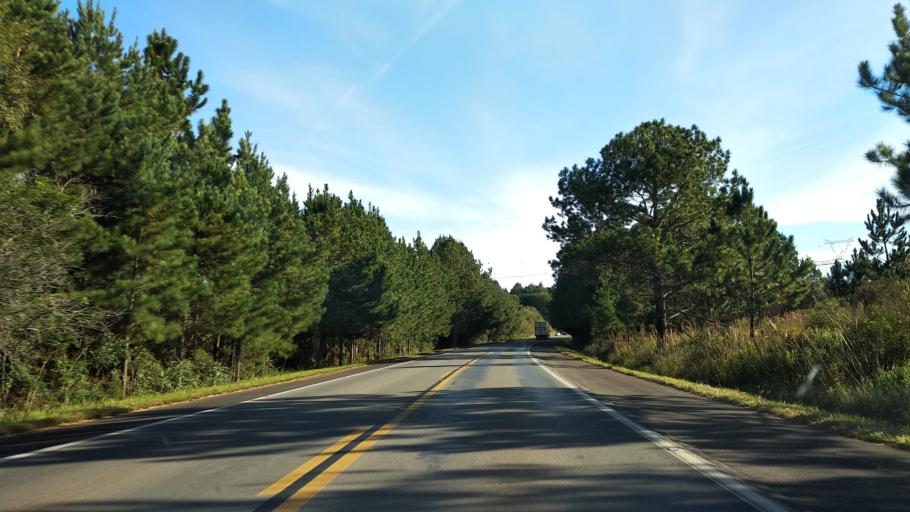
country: BR
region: Santa Catarina
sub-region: Celso Ramos
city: Celso Ramos
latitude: -27.5371
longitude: -51.4051
